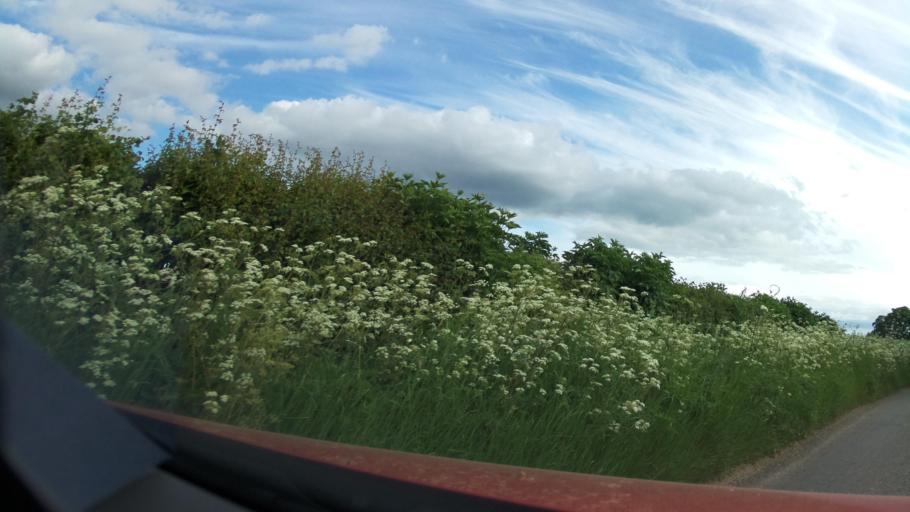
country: GB
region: England
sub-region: Gloucestershire
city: Moreton in Marsh
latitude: 52.0083
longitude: -1.7242
